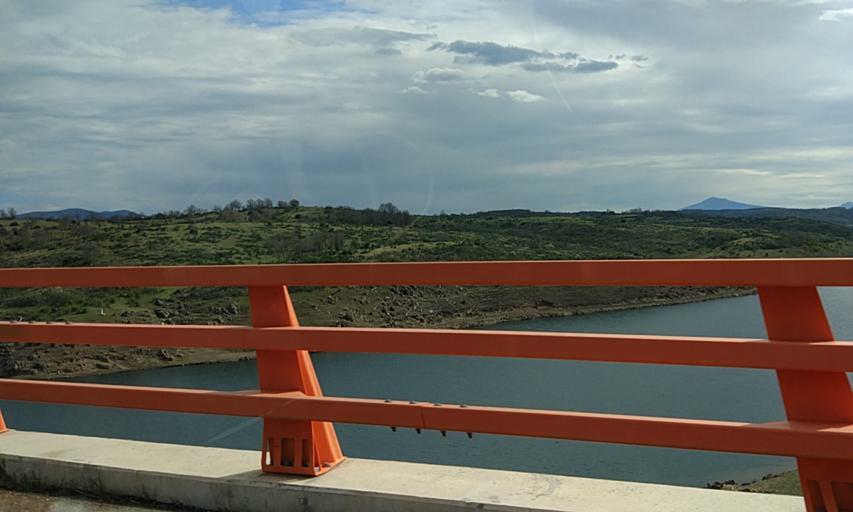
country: ES
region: Castille and Leon
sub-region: Provincia de Salamanca
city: Robleda
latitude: 40.4298
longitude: -6.6034
